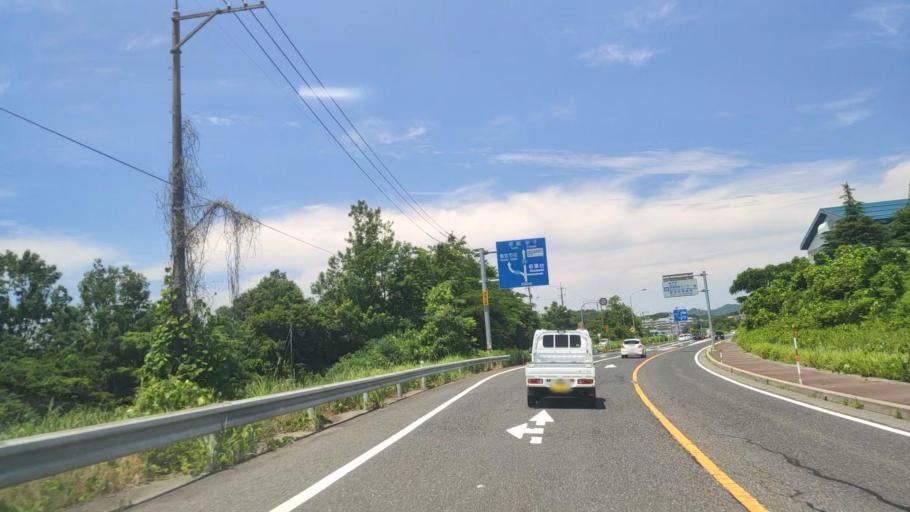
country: JP
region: Tottori
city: Tottori
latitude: 35.4404
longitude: 134.2558
